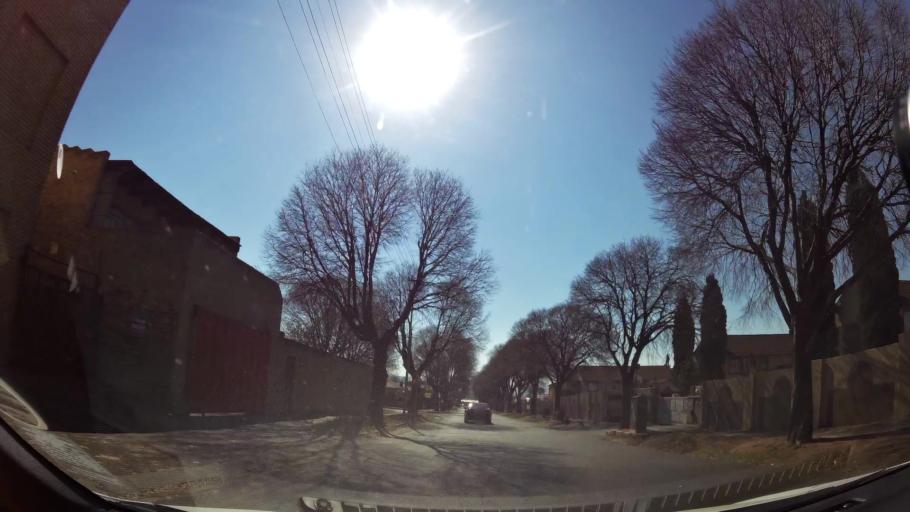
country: ZA
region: Gauteng
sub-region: City of Johannesburg Metropolitan Municipality
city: Johannesburg
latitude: -26.2426
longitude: 28.0763
